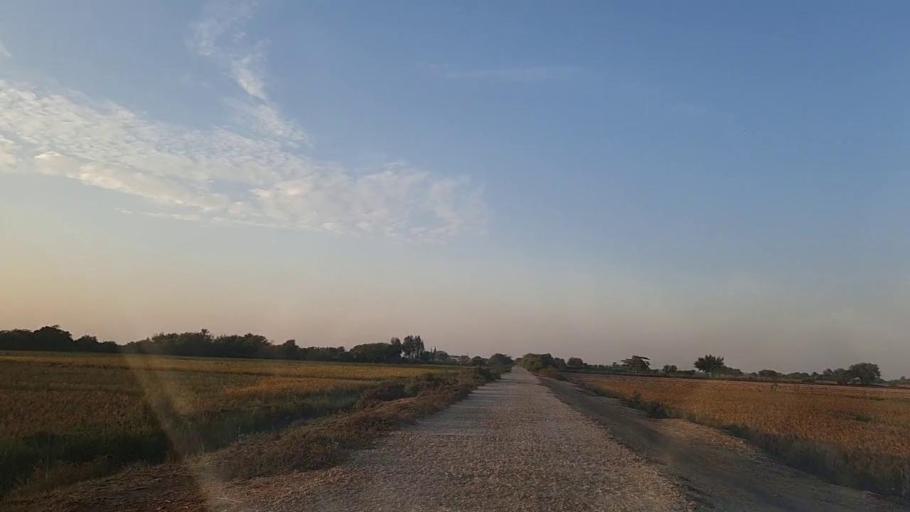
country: PK
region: Sindh
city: Chuhar Jamali
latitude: 24.4513
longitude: 68.1182
